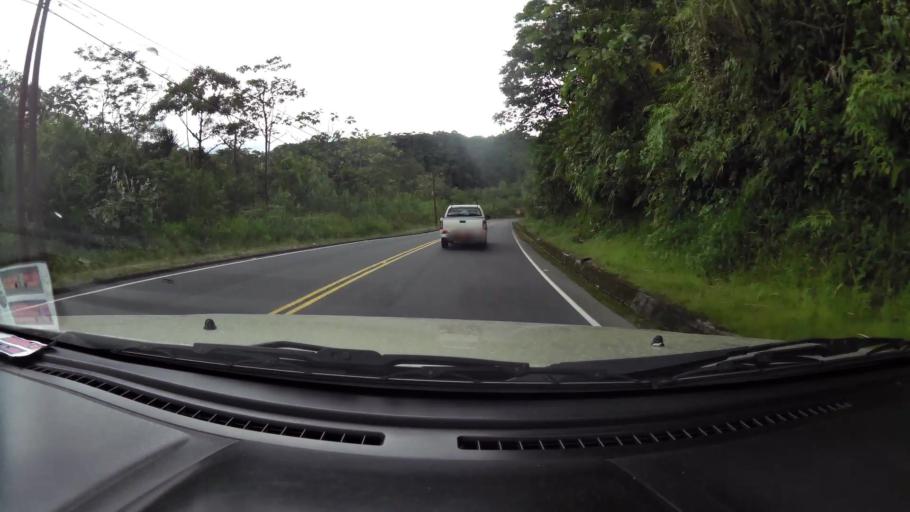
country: EC
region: Pastaza
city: Puyo
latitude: -1.4655
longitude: -78.1055
